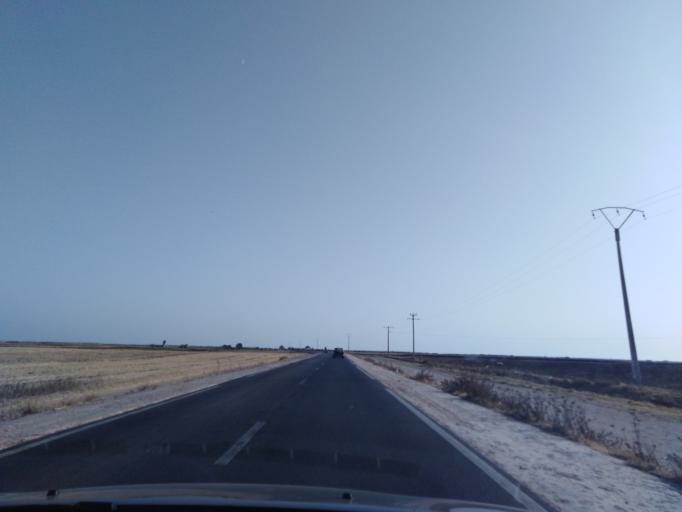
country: MA
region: Doukkala-Abda
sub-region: El-Jadida
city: Sidi Bennour
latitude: 32.5300
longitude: -8.7352
